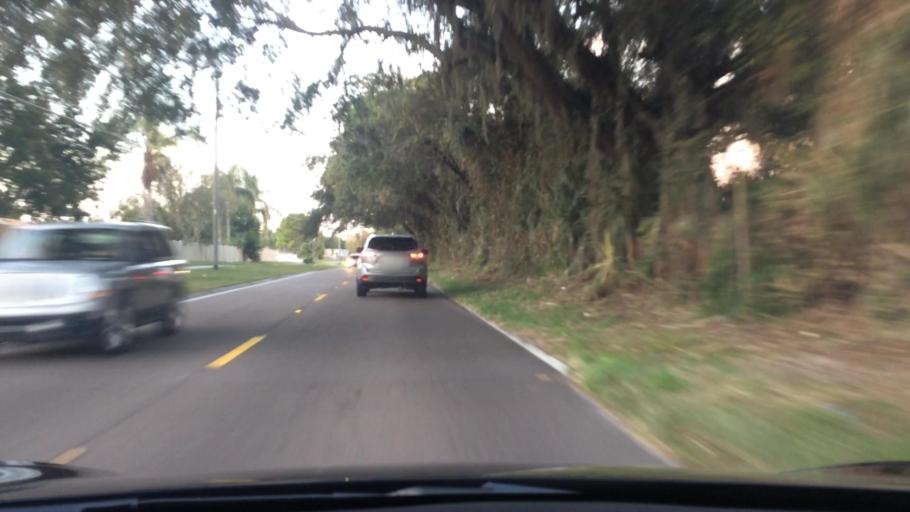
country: US
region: Florida
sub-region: Hillsborough County
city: Lutz
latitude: 28.1791
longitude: -82.4032
